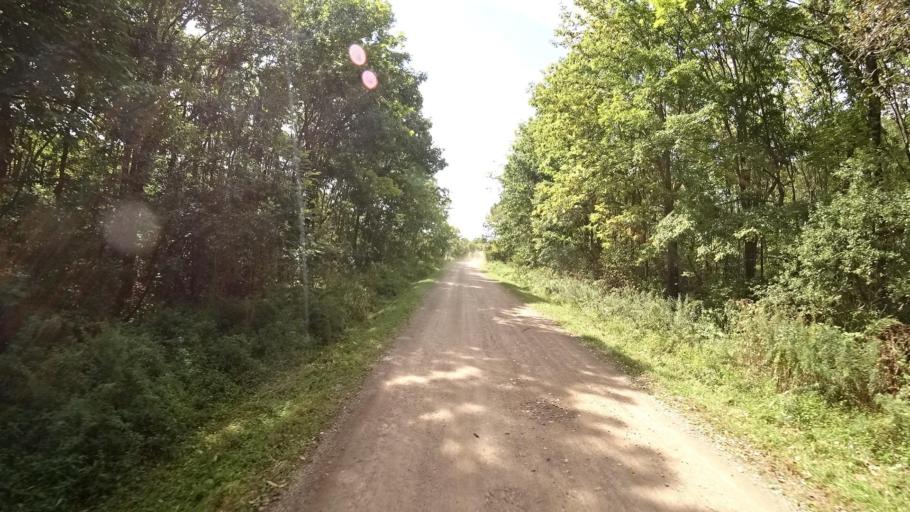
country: RU
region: Primorskiy
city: Yakovlevka
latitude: 44.6600
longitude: 133.7485
